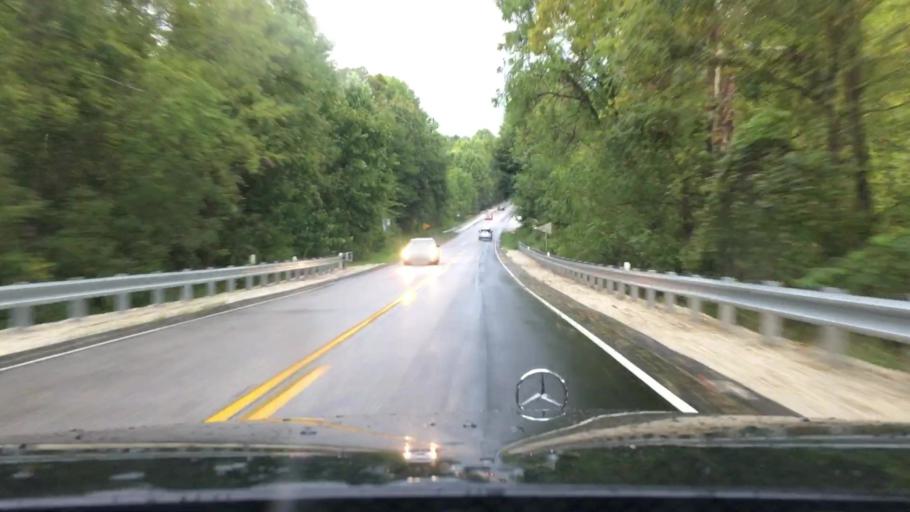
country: US
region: Virginia
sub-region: Amherst County
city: Amherst
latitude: 37.6928
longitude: -79.0281
